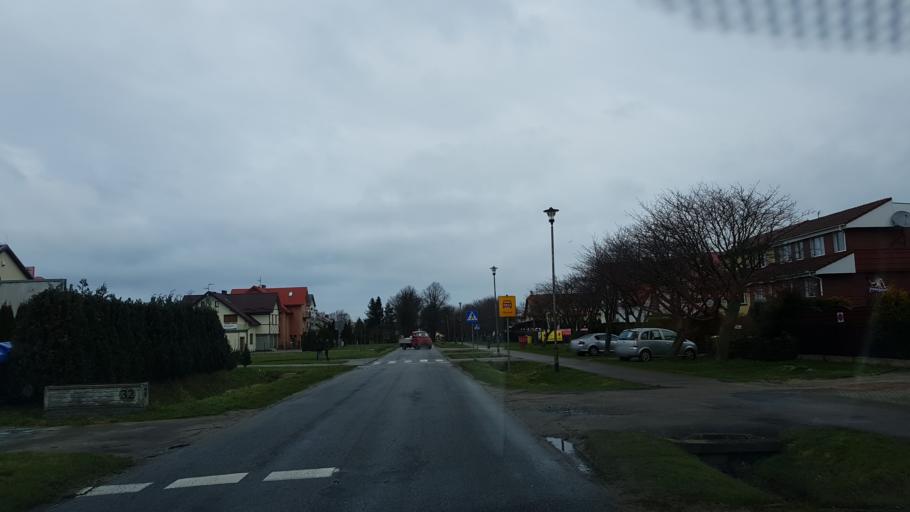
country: PL
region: West Pomeranian Voivodeship
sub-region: Powiat kolobrzeski
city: Ustronie Morskie
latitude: 54.2081
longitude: 15.7471
